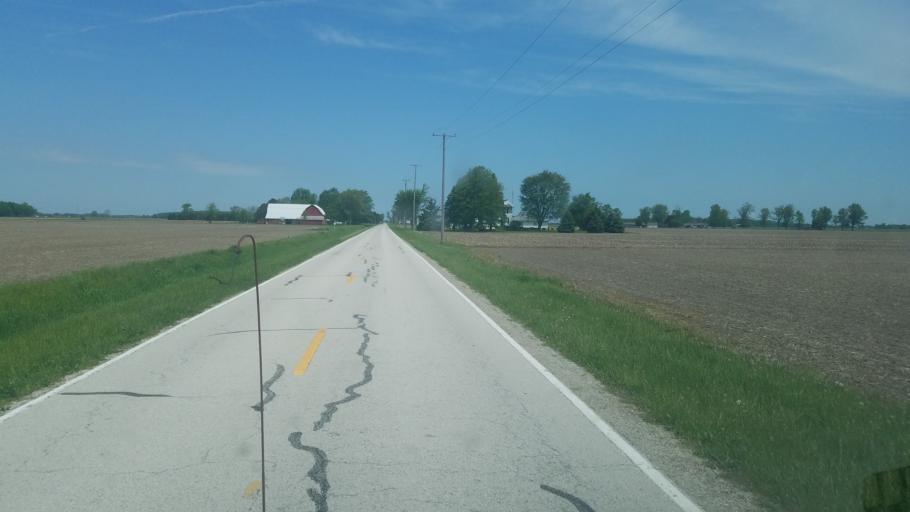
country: US
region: Ohio
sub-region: Ottawa County
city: Oak Harbor
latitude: 41.4386
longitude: -83.2015
